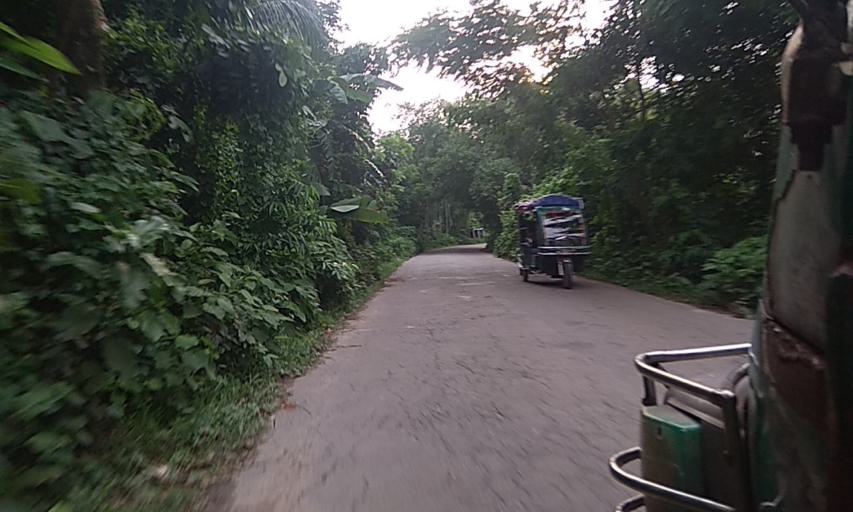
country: BD
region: Dhaka
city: Dohar
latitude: 23.4576
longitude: 90.0012
